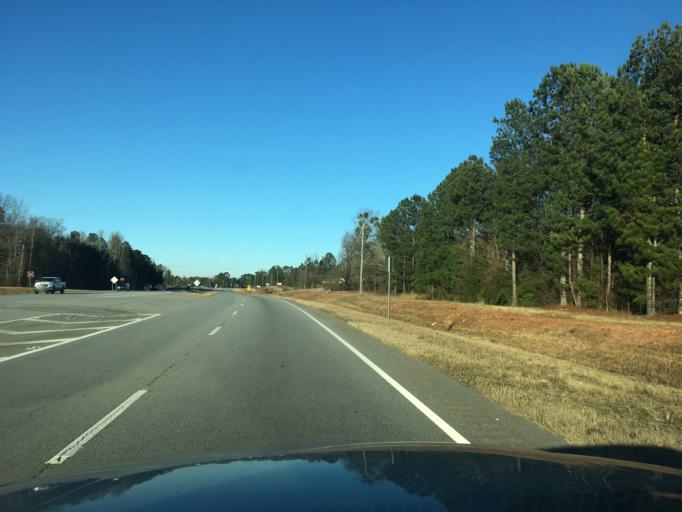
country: US
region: Georgia
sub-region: Carroll County
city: Carrollton
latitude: 33.5006
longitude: -85.0816
